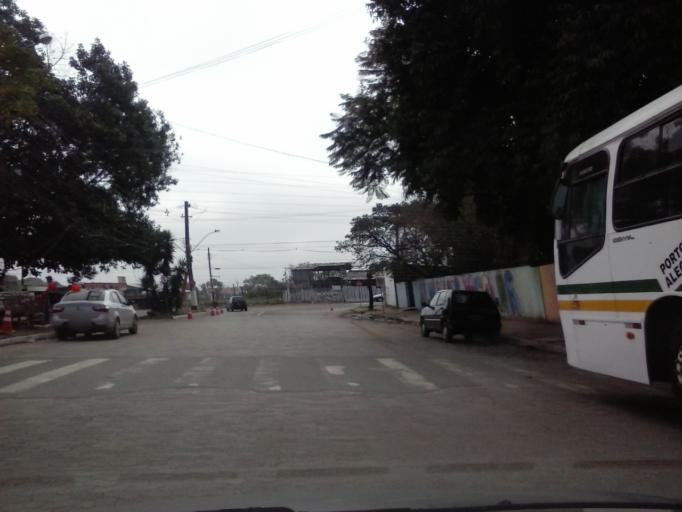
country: BR
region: Rio Grande do Sul
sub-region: Viamao
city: Viamao
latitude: -30.0470
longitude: -51.0852
